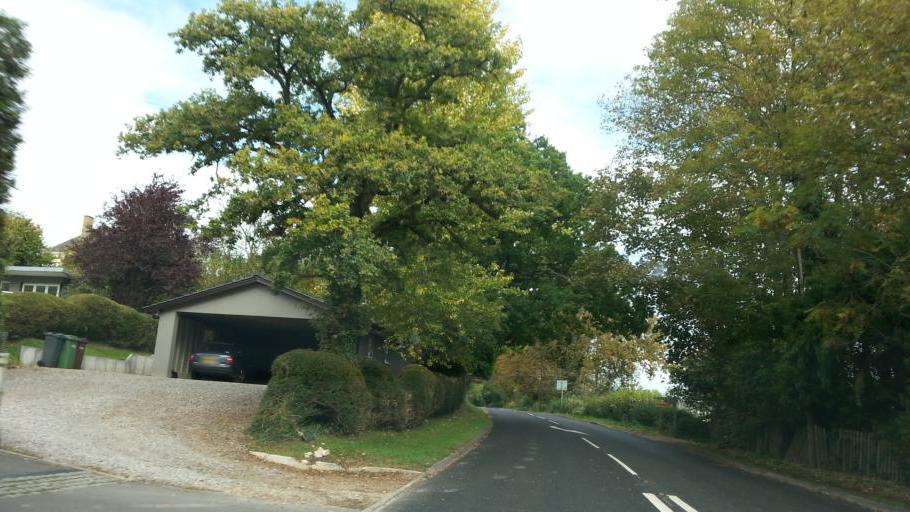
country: GB
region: England
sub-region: Gloucestershire
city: Painswick
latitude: 51.7708
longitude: -2.2146
